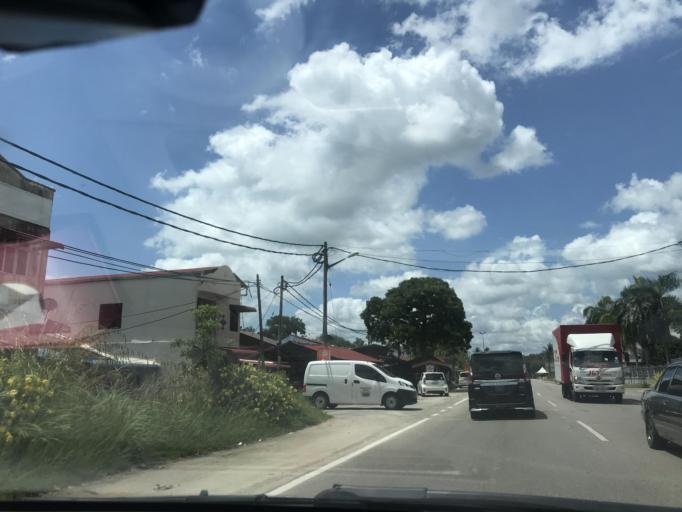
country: TH
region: Narathiwat
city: Tak Bai
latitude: 6.2281
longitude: 102.0953
